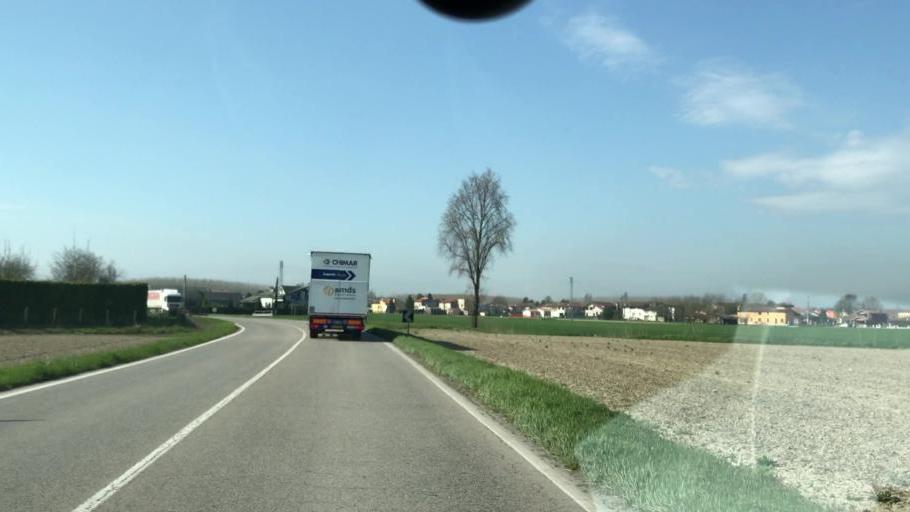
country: IT
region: Veneto
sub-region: Provincia di Rovigo
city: Castelnovo Bariano
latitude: 45.0279
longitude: 11.2973
